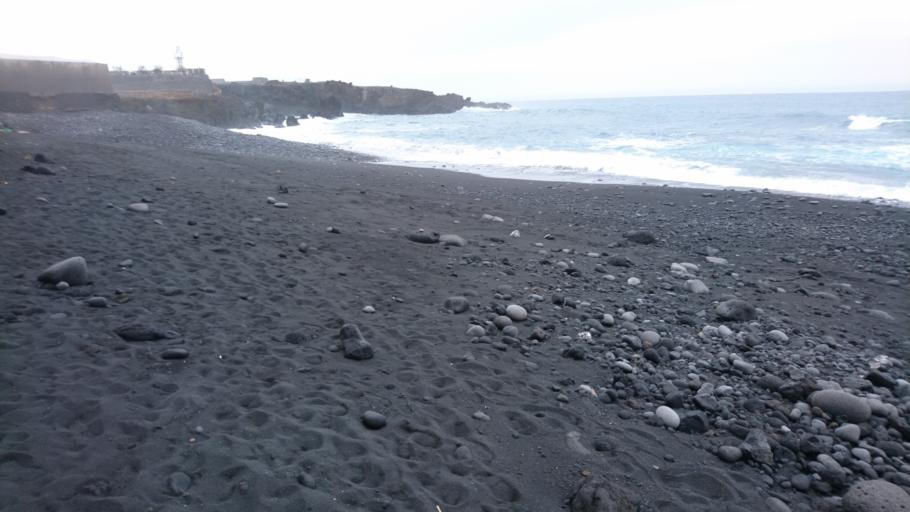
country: ES
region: Canary Islands
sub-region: Provincia de Santa Cruz de Tenerife
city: Tazacorte
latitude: 28.6018
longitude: -17.9234
